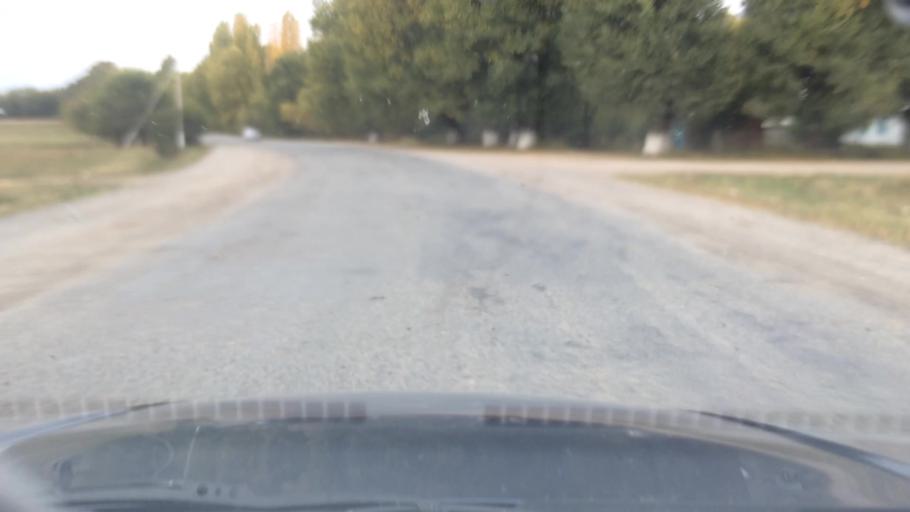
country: KG
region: Ysyk-Koel
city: Tyup
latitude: 42.7871
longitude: 78.2626
